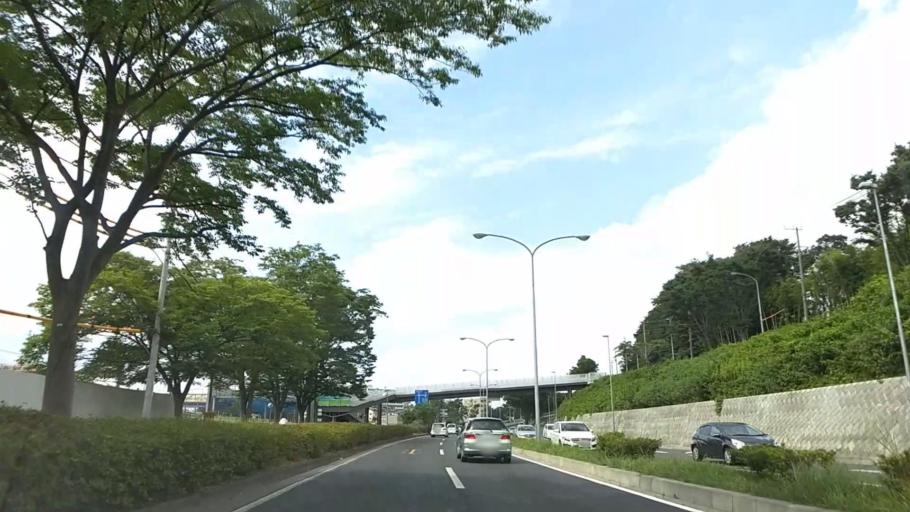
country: JP
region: Kanagawa
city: Yokohama
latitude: 35.4826
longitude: 139.5874
